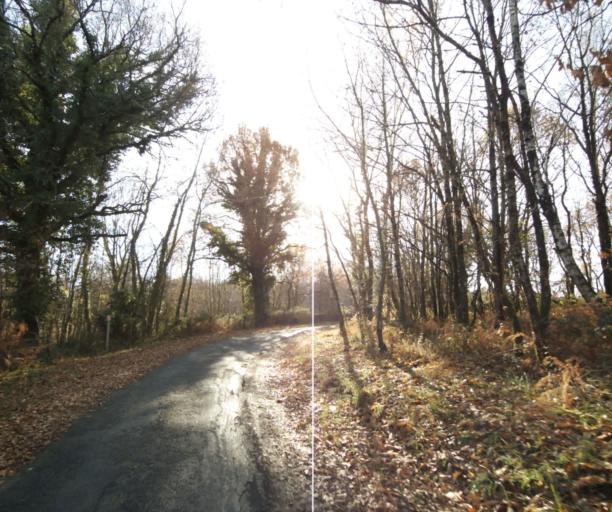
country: FR
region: Poitou-Charentes
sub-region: Departement de la Charente-Maritime
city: Burie
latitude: 45.7532
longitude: -0.4824
